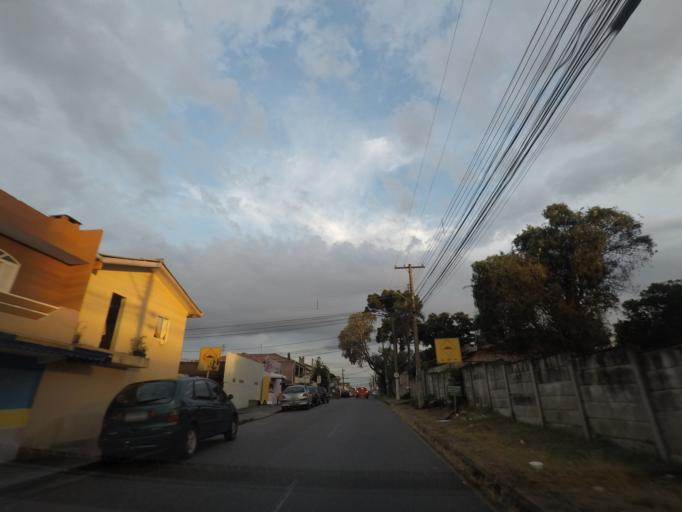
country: BR
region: Parana
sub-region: Sao Jose Dos Pinhais
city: Sao Jose dos Pinhais
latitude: -25.5054
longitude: -49.2506
